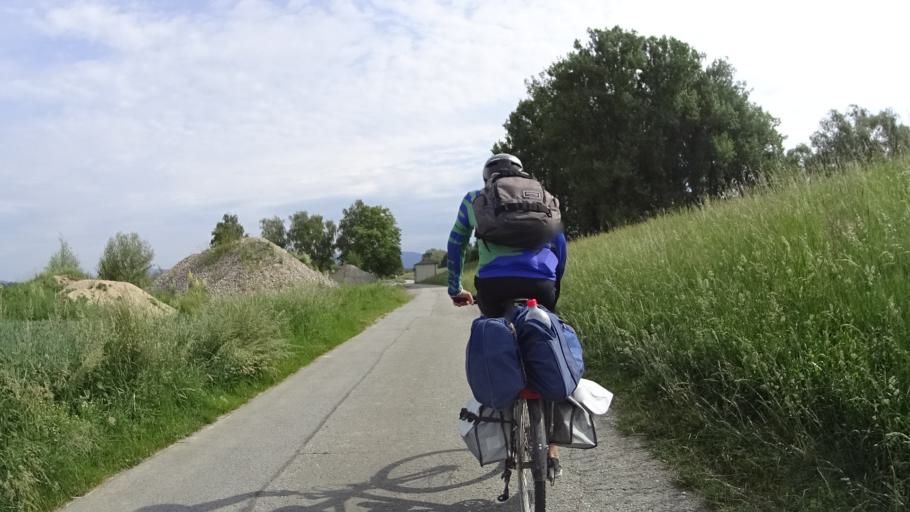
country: DE
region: Bavaria
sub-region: Lower Bavaria
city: Mariaposching
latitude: 48.8342
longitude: 12.8374
